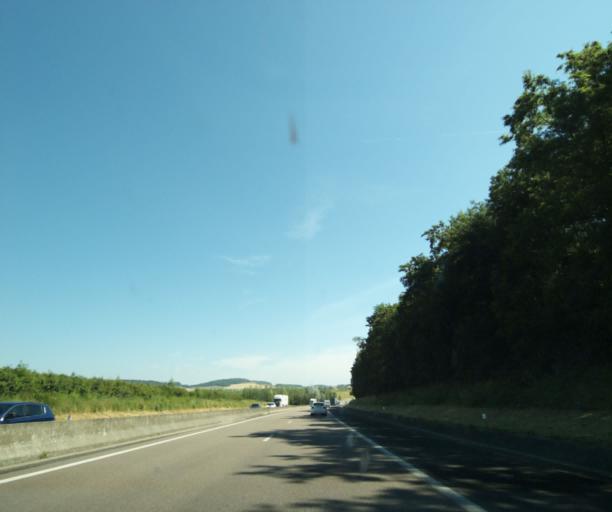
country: FR
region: Lorraine
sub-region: Departement des Vosges
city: Chatenois
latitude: 48.3463
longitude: 5.8550
